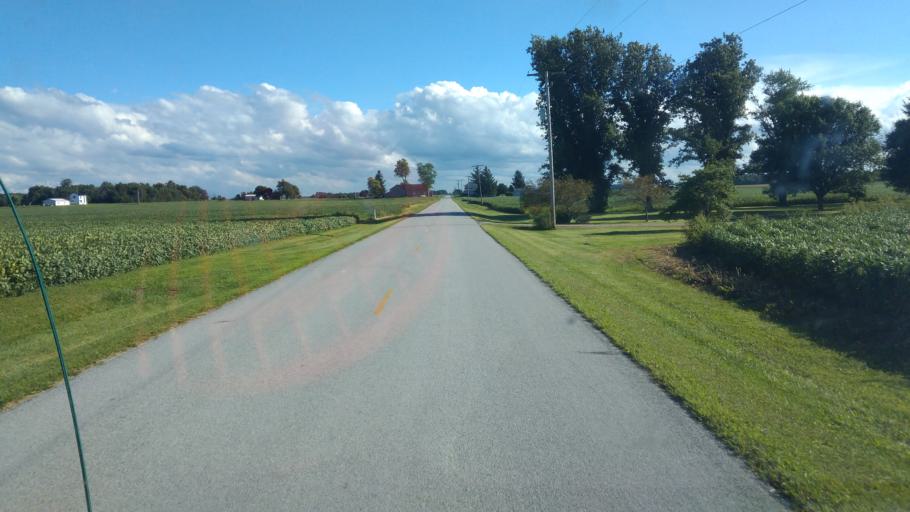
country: US
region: Ohio
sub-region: Hardin County
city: Ada
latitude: 40.7659
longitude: -83.6903
